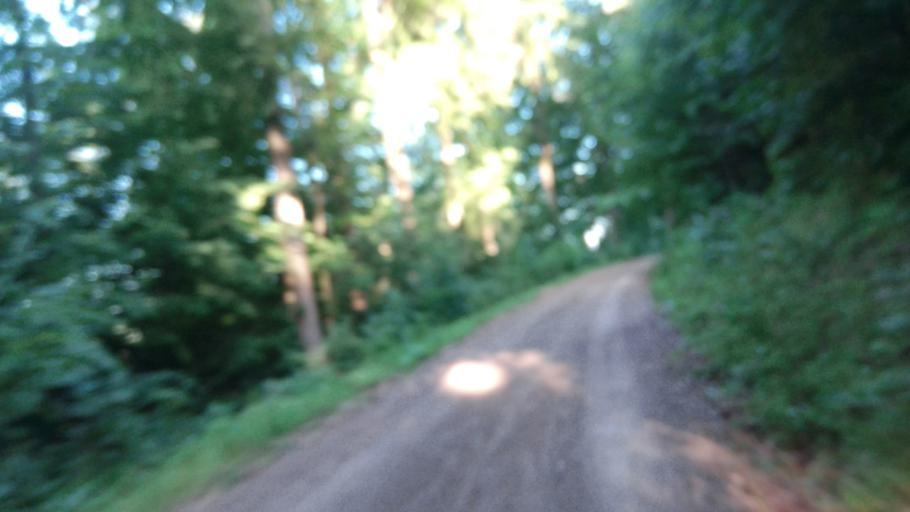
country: DE
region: Lower Saxony
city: Salzhemmendorf
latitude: 52.0323
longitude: 9.5834
